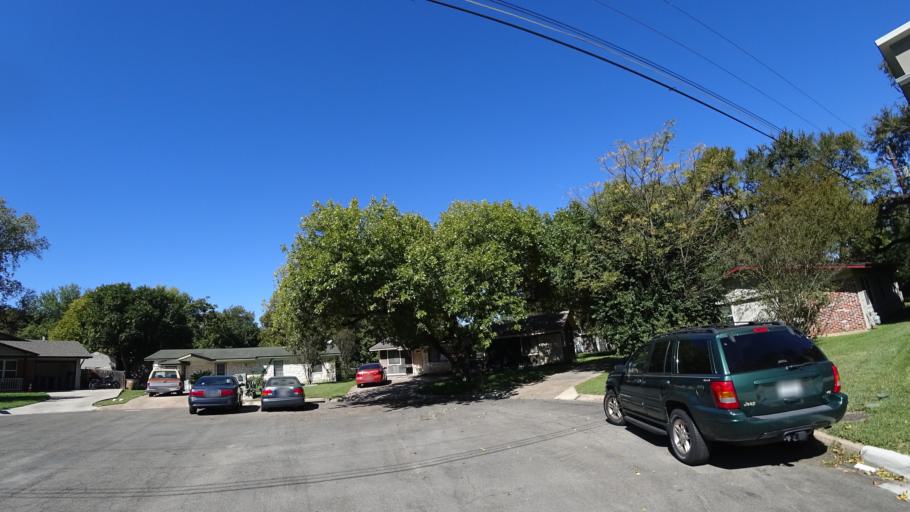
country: US
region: Texas
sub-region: Travis County
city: Austin
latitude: 30.2341
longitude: -97.7716
